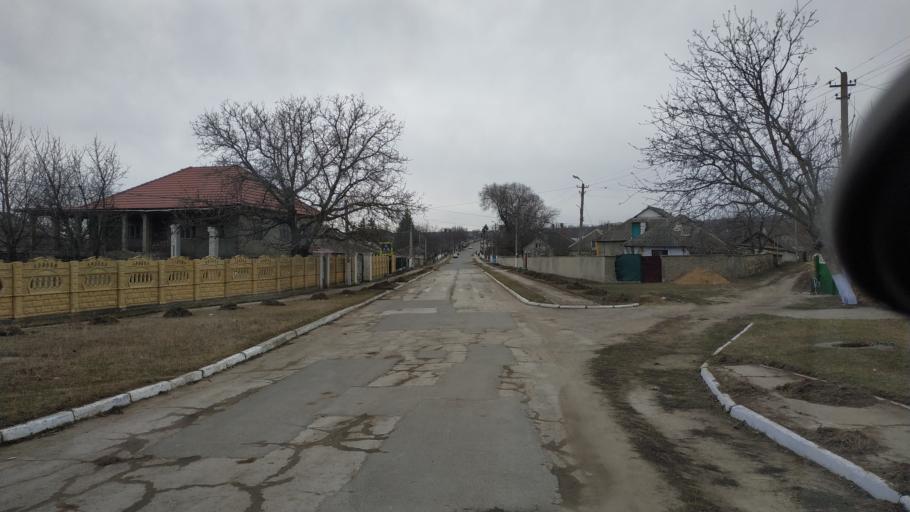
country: MD
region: Telenesti
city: Cocieri
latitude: 47.2592
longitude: 29.0667
